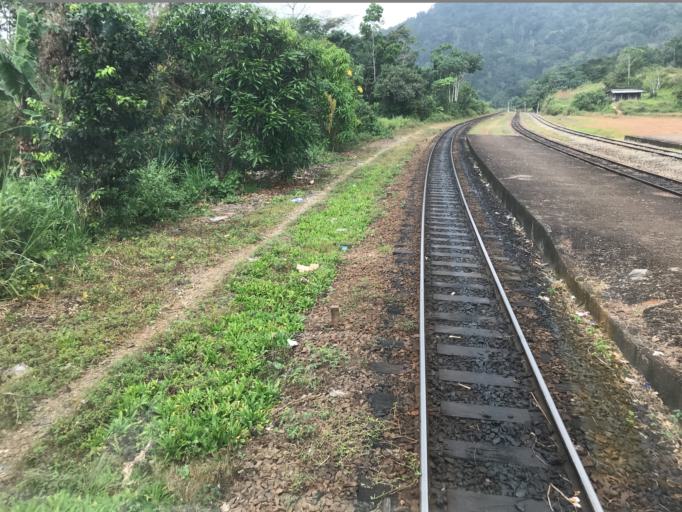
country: CM
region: Centre
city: Eseka
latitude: 3.5726
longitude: 10.8991
